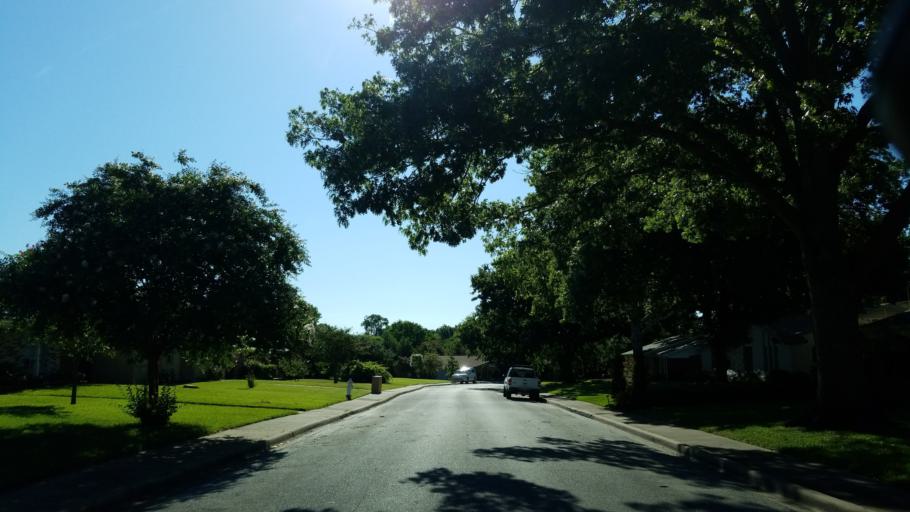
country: US
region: Texas
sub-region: Dallas County
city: Carrollton
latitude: 32.9449
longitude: -96.8864
